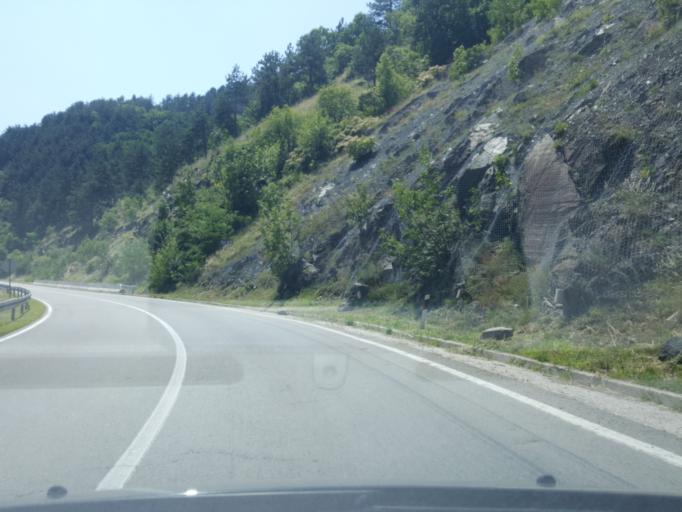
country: RS
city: Prislonica
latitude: 43.9875
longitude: 20.4176
